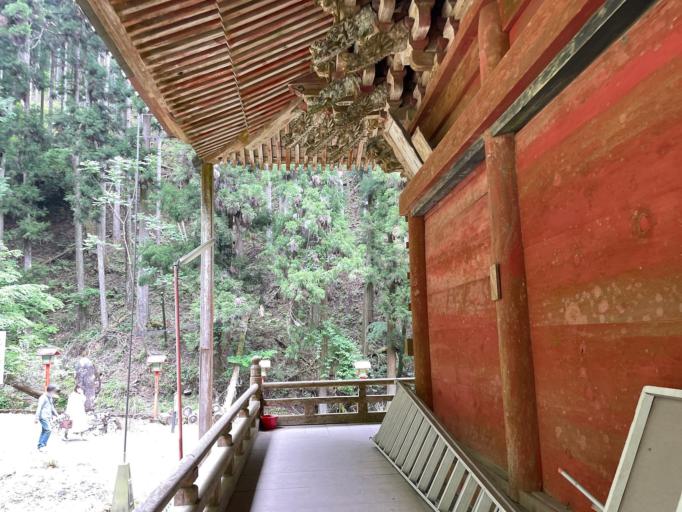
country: JP
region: Tochigi
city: Tanuma
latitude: 36.4756
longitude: 139.5891
